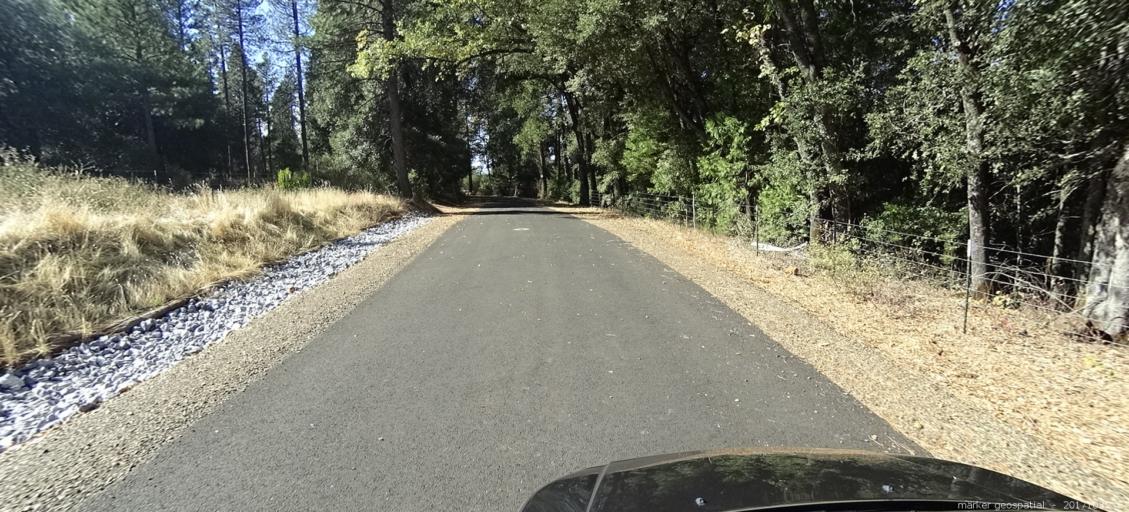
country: US
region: California
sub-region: Shasta County
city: Shingletown
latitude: 40.5320
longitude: -121.9448
